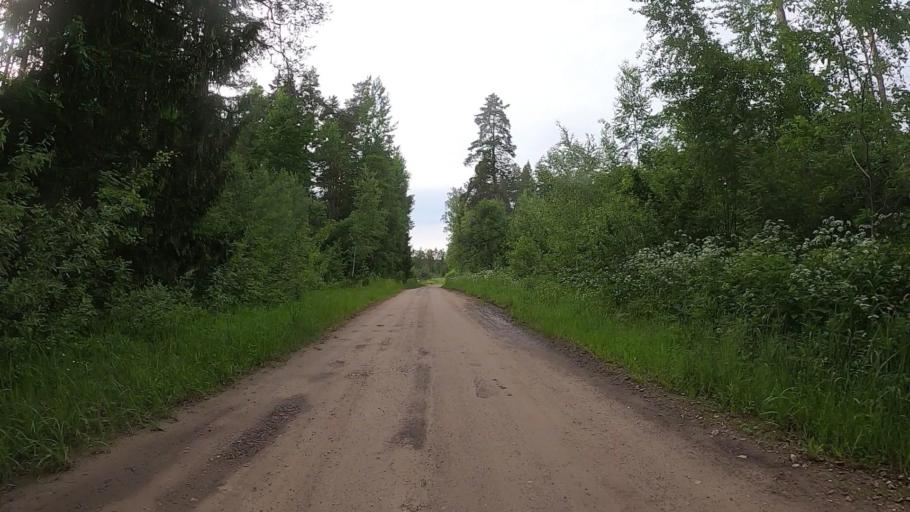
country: LV
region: Ozolnieku
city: Ozolnieki
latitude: 56.7260
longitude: 23.7893
